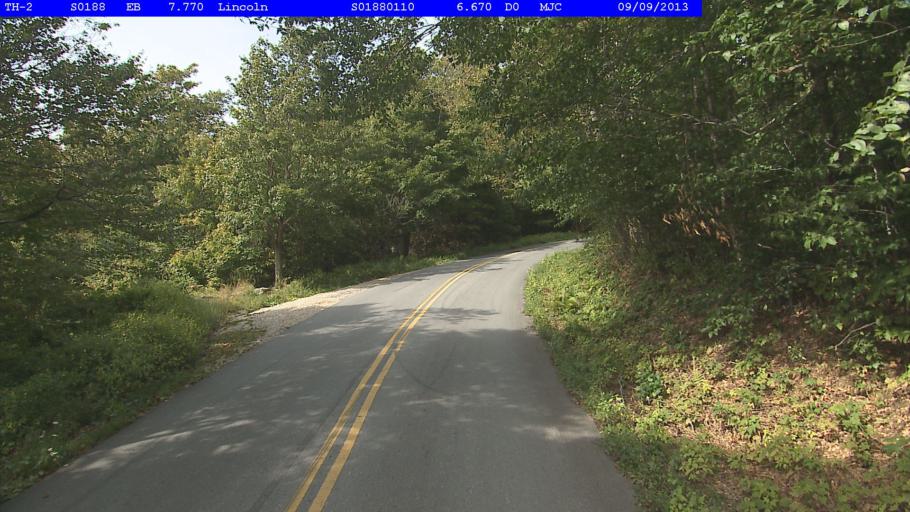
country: US
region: Vermont
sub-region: Addison County
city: Bristol
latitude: 44.0944
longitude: -72.9328
